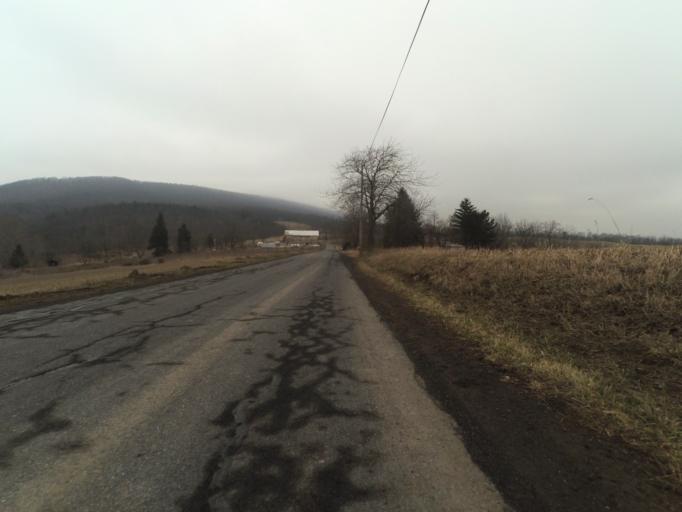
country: US
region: Pennsylvania
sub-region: Centre County
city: Centre Hall
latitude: 40.8698
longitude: -77.5962
